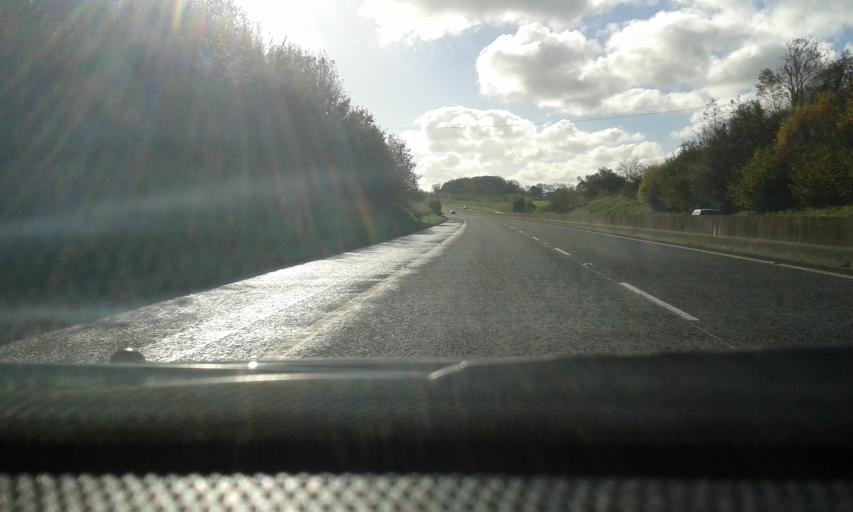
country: IE
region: Munster
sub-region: County Cork
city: Rathcormac
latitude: 52.0757
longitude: -8.3013
